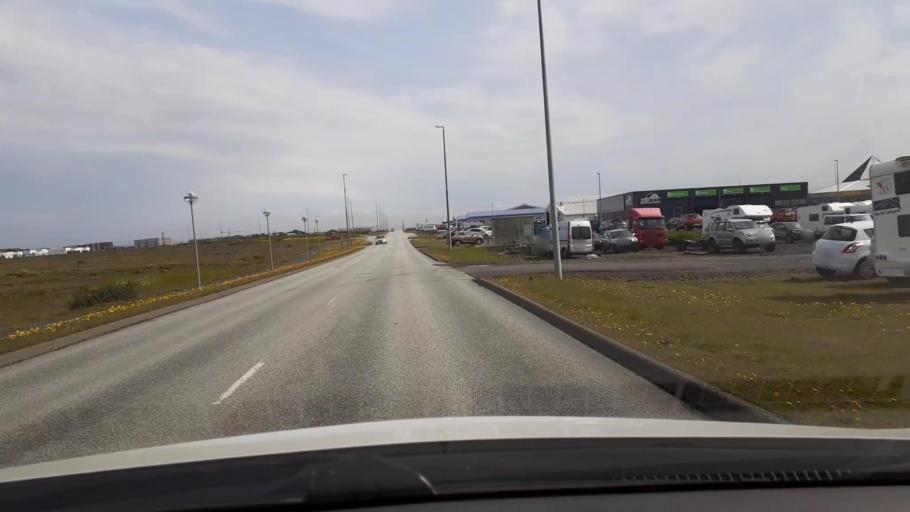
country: IS
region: Southern Peninsula
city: Reykjanesbaer
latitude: 63.9724
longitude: -22.5339
